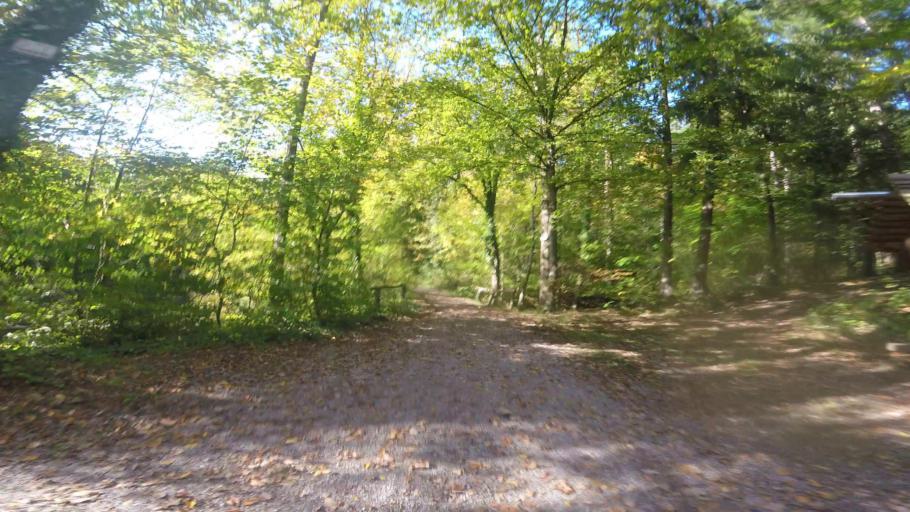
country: DE
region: Baden-Wuerttemberg
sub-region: Regierungsbezirk Stuttgart
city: Oberstenfeld
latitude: 48.9921
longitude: 9.3284
